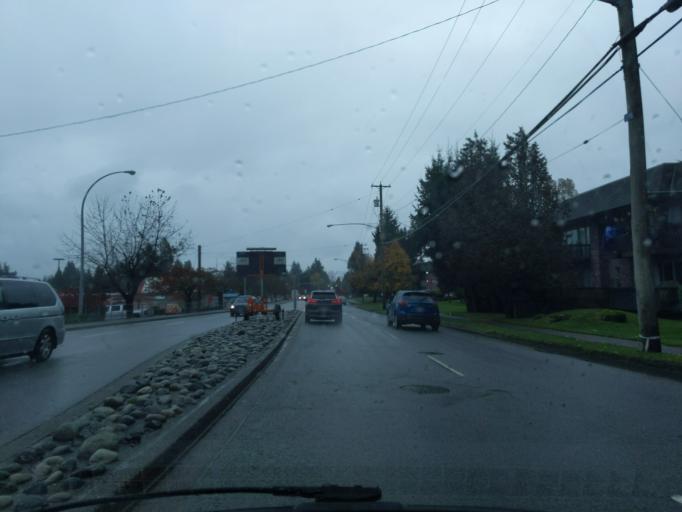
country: CA
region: British Columbia
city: Surrey
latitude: 49.1982
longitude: -122.8105
